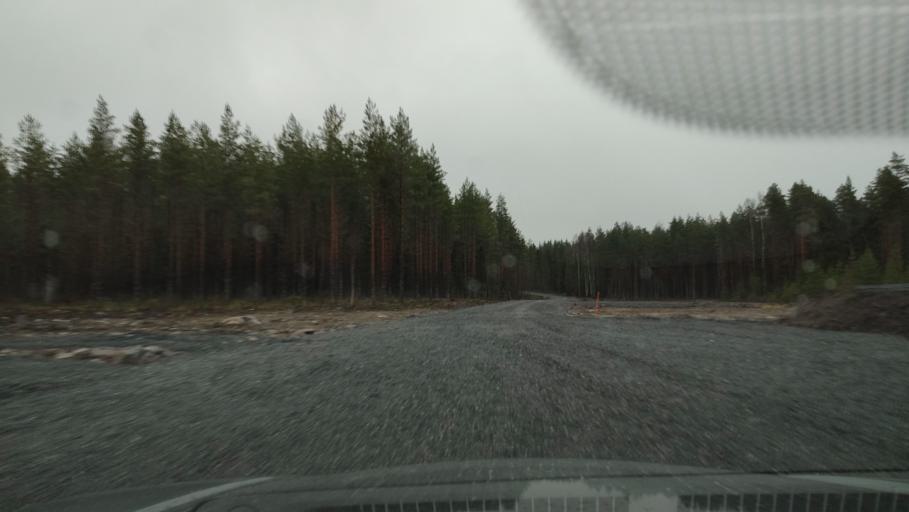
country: FI
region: Southern Ostrobothnia
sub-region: Suupohja
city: Karijoki
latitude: 62.1542
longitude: 21.6064
